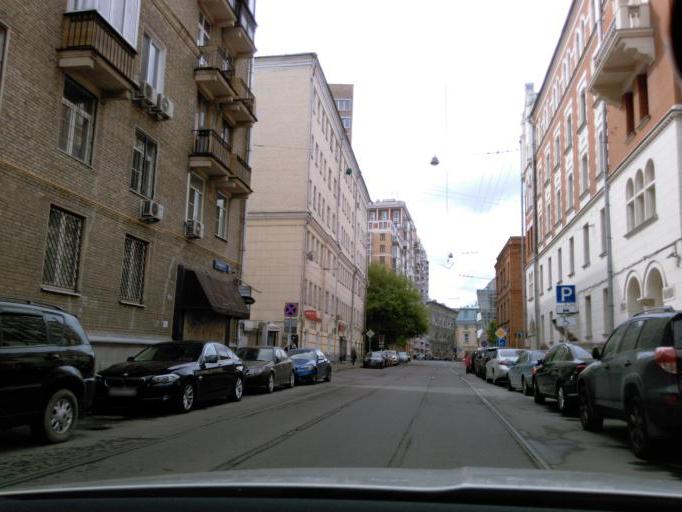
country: RU
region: Moscow
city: Mar'ina Roshcha
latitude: 55.7872
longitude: 37.6330
